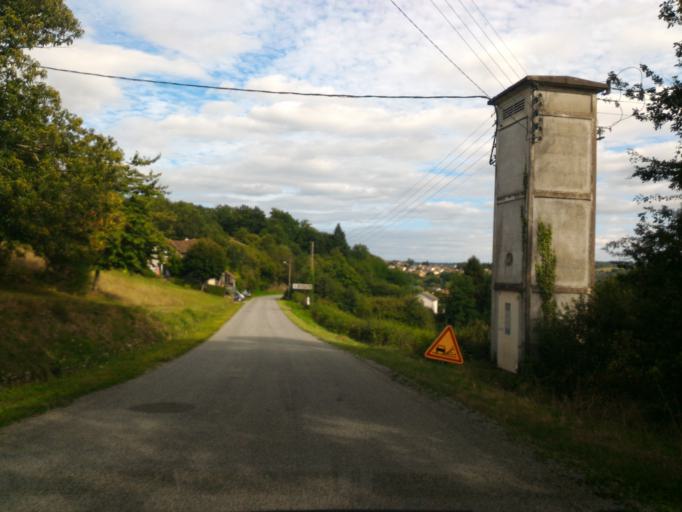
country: FR
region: Limousin
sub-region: Departement de la Haute-Vienne
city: Saint-Junien
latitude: 45.8952
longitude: 0.8806
